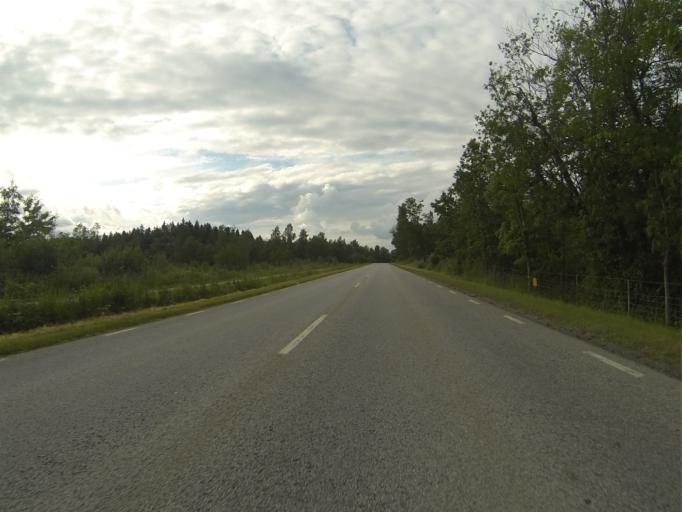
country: SE
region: Skane
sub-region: Lunds Kommun
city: Genarp
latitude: 55.6987
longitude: 13.3473
